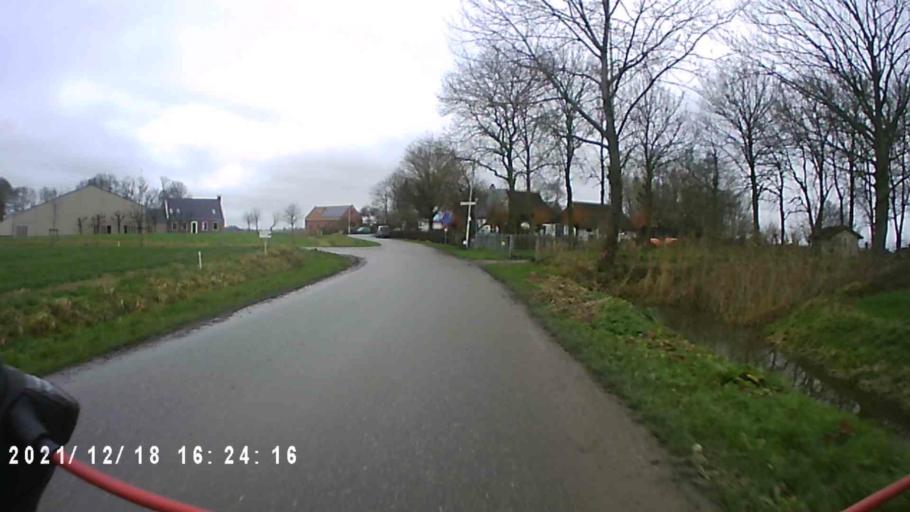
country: NL
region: Friesland
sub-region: Gemeente Dongeradeel
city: Dokkum
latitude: 53.3798
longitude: 6.0362
